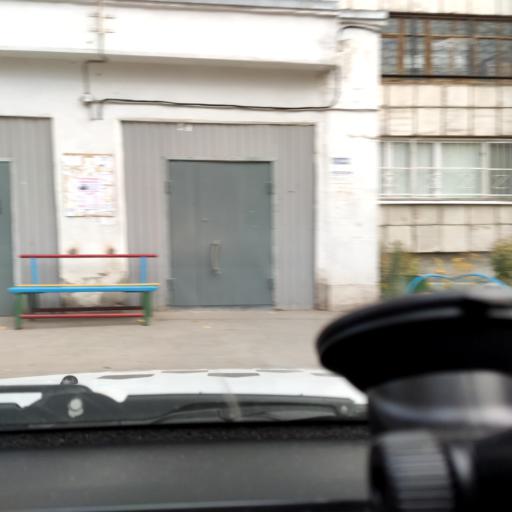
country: RU
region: Perm
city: Perm
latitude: 58.0249
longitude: 56.3051
